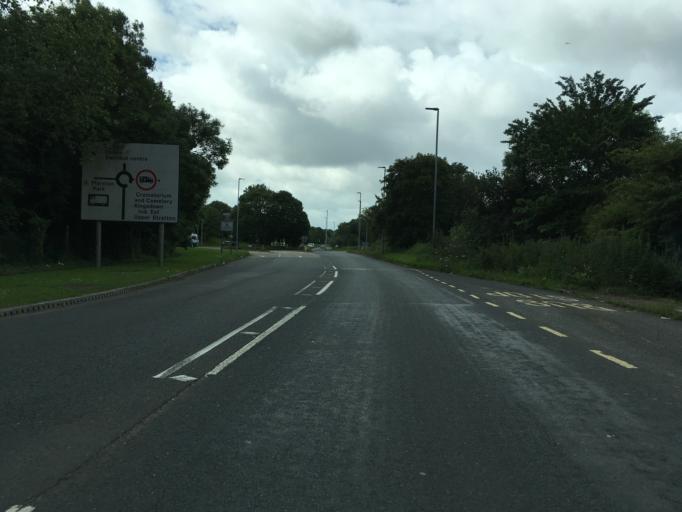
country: GB
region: England
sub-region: Borough of Swindon
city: Hannington
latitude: 51.5997
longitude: -1.7415
